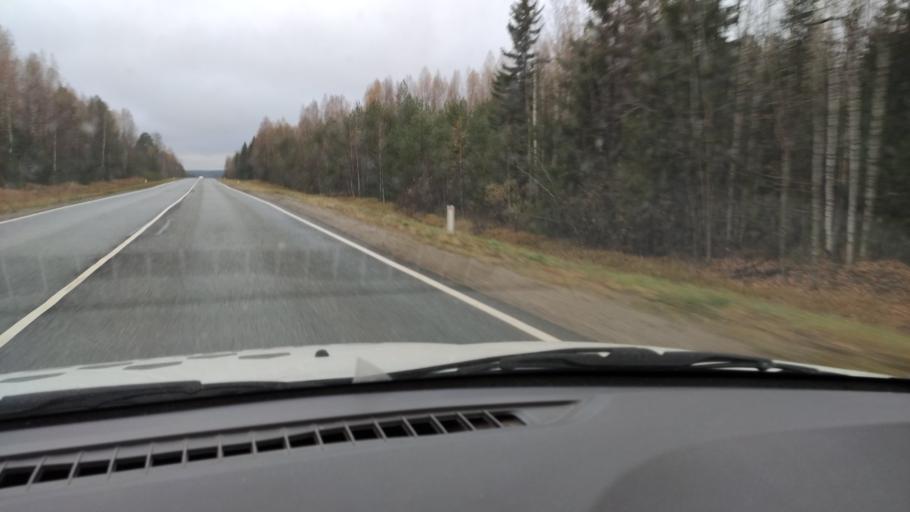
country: RU
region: Kirov
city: Dubrovka
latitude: 58.8979
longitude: 51.3169
